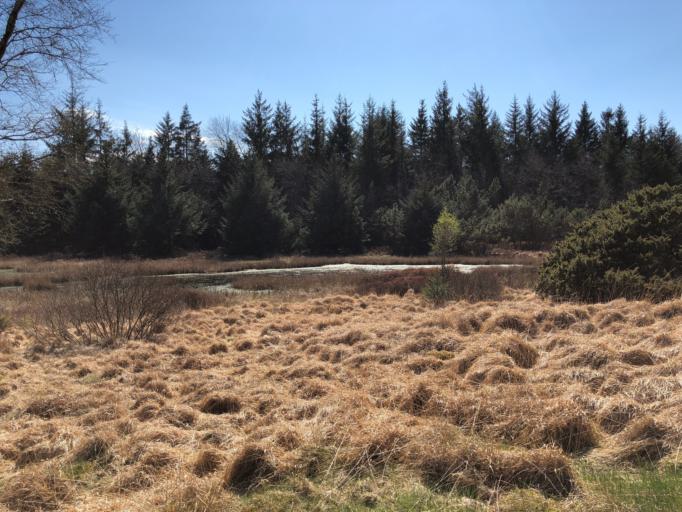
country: DK
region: Central Jutland
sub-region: Holstebro Kommune
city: Ulfborg
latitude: 56.2372
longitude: 8.4056
